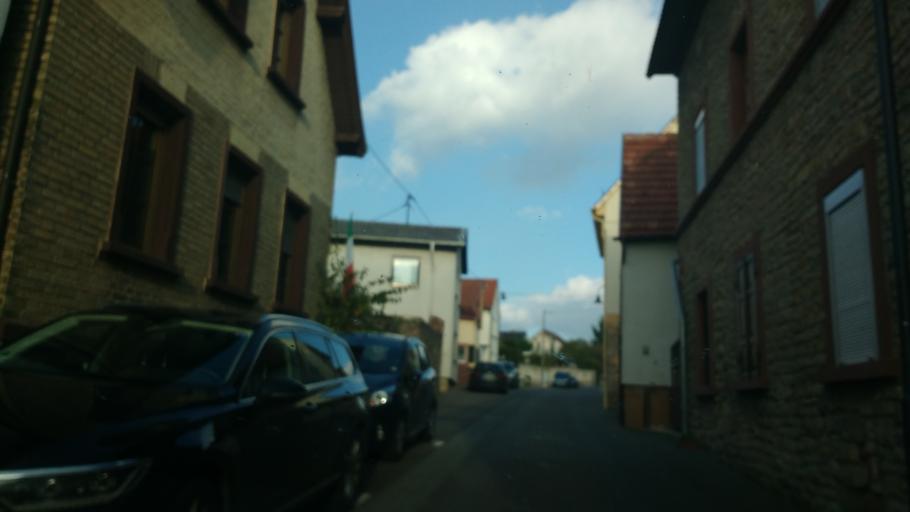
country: DE
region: Rheinland-Pfalz
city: Offstein
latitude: 49.6070
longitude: 8.2375
